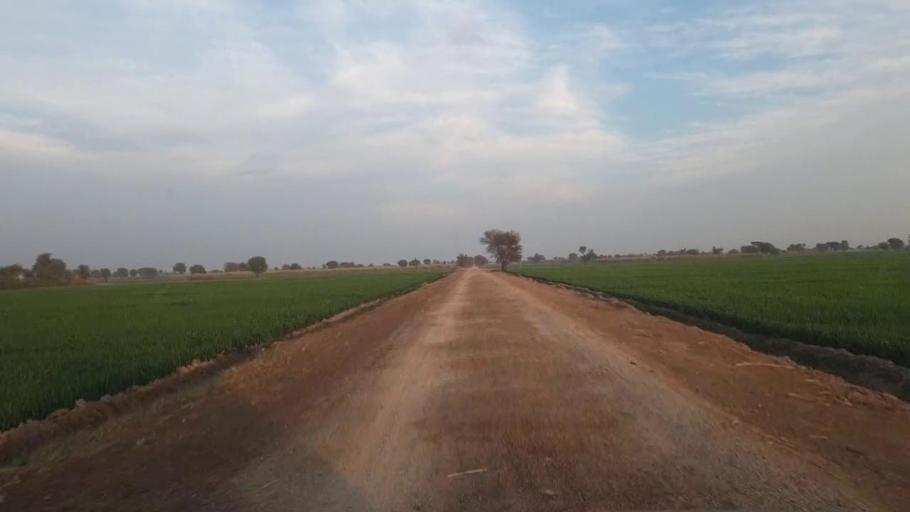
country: PK
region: Sindh
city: Shahdadpur
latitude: 26.0528
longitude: 68.5341
